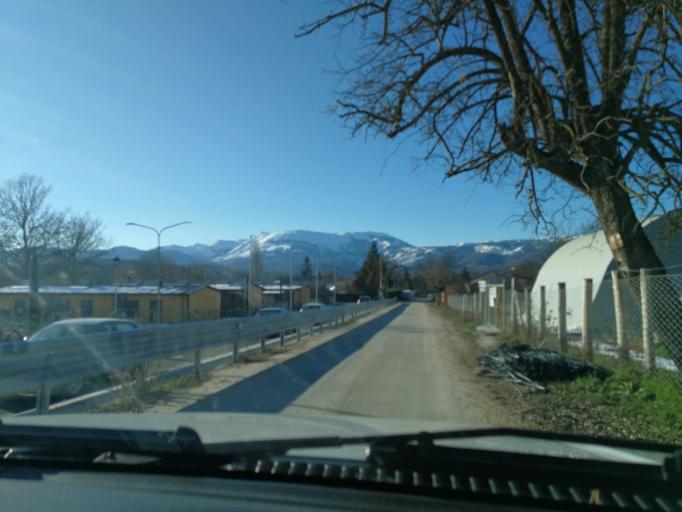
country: IT
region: Latium
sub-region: Provincia di Rieti
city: Amatrice
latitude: 42.6564
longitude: 13.2899
